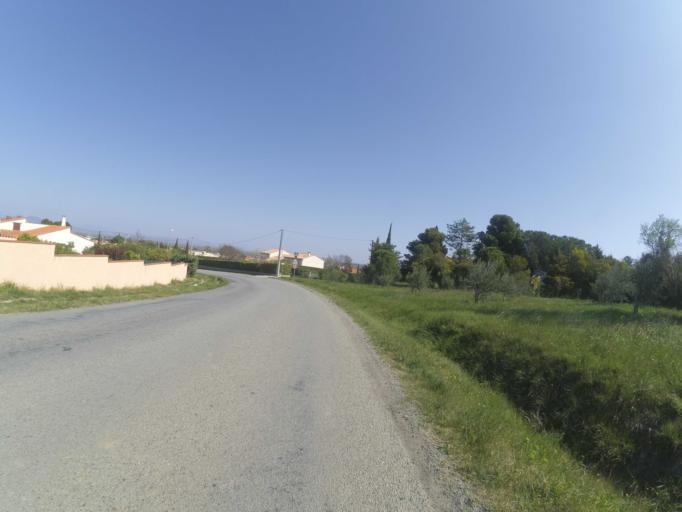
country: FR
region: Languedoc-Roussillon
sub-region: Departement des Pyrenees-Orientales
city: Llupia
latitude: 42.6129
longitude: 2.7699
